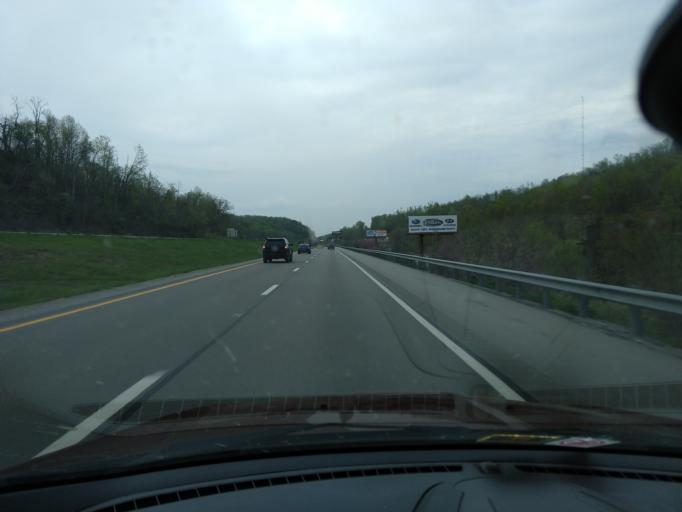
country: US
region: West Virginia
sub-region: Lewis County
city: Weston
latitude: 39.1318
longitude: -80.3803
